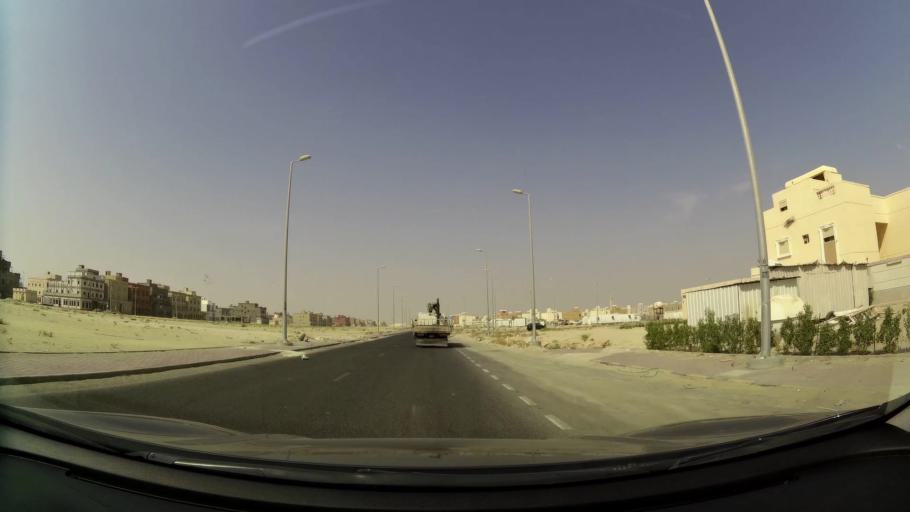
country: KW
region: Al Ahmadi
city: Al Wafrah
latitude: 28.7976
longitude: 48.0610
